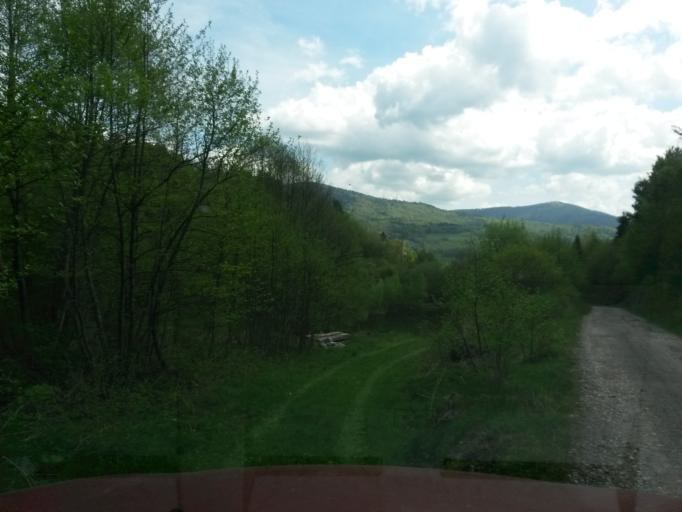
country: SK
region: Kosicky
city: Krompachy
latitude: 48.8148
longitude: 20.8044
